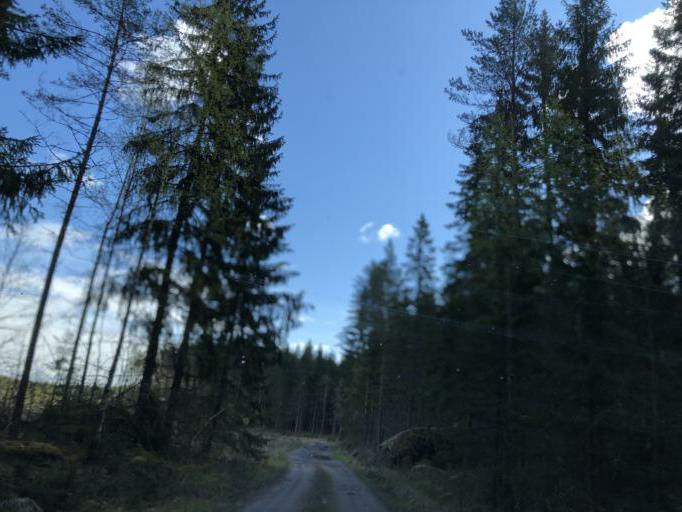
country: SE
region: Uppsala
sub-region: Heby Kommun
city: Tarnsjo
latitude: 60.2326
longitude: 16.7135
